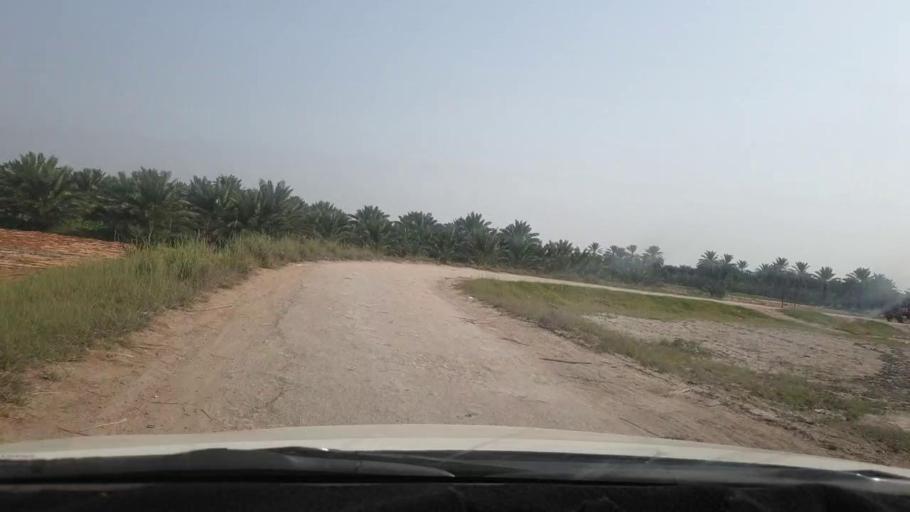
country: PK
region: Sindh
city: Rohri
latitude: 27.5892
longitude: 68.8740
